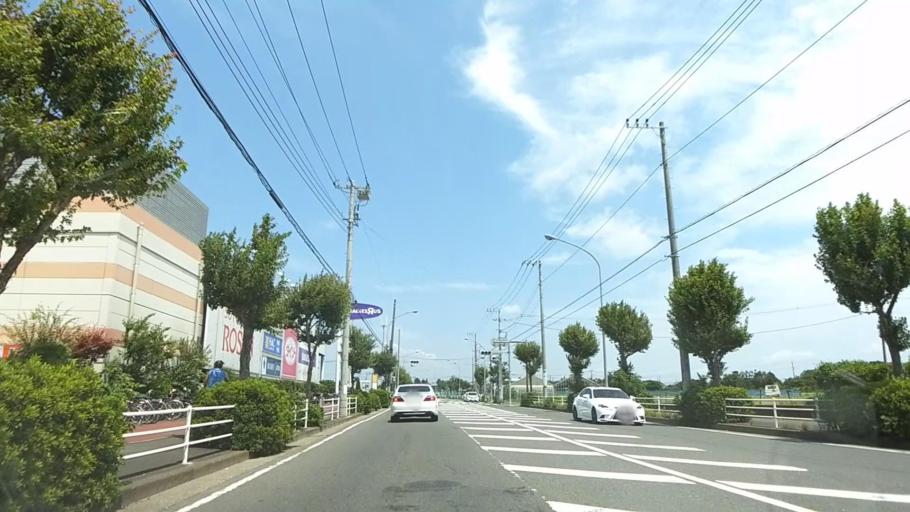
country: JP
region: Kanagawa
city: Minami-rinkan
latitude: 35.4474
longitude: 139.4840
